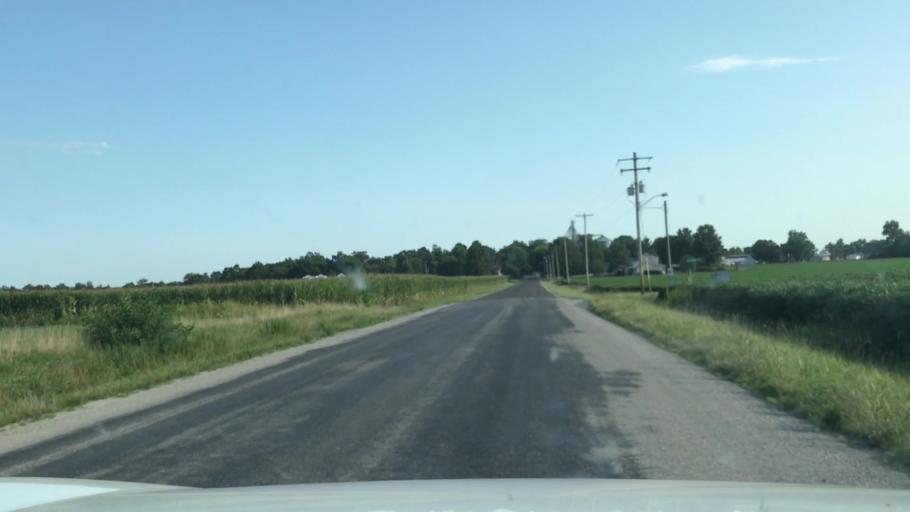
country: US
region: Illinois
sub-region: Washington County
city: Okawville
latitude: 38.3986
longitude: -89.4864
